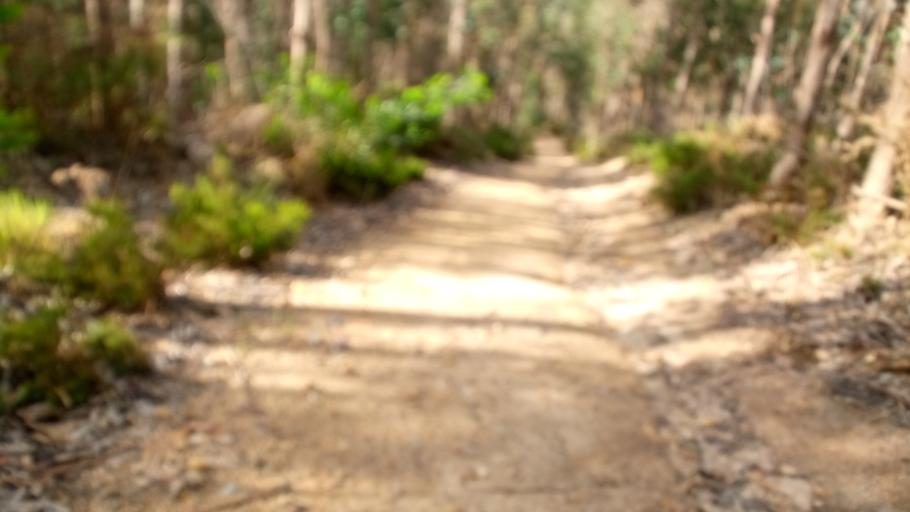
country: PT
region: Leiria
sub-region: Obidos
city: Obidos
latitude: 39.3905
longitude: -9.2087
